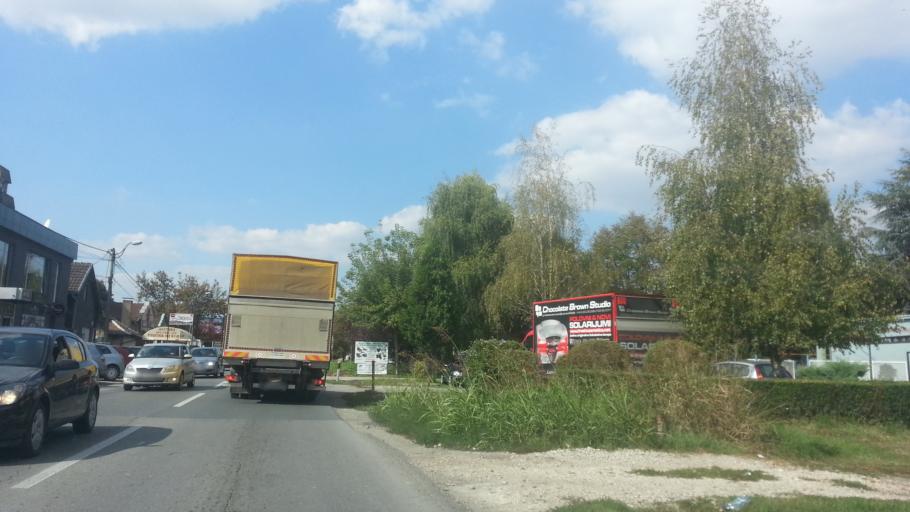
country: RS
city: Novi Banovci
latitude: 44.8963
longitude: 20.2936
